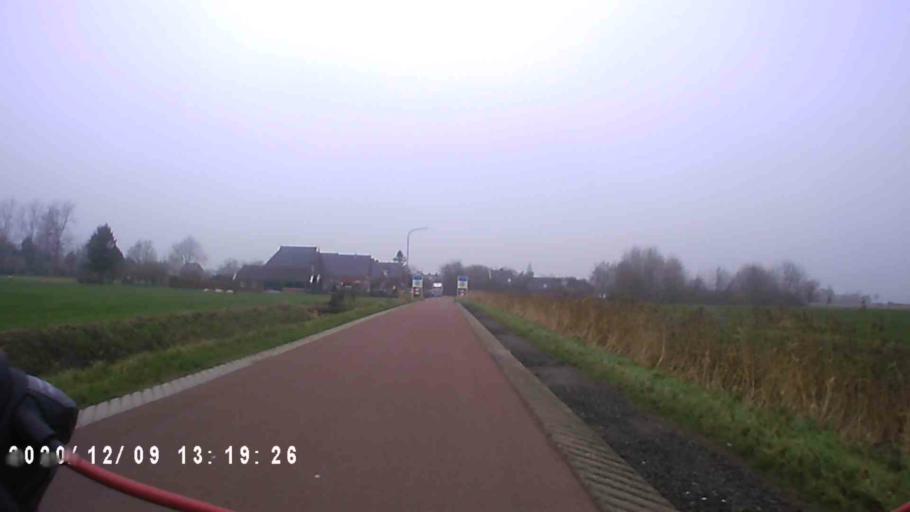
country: NL
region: Groningen
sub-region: Gemeente Groningen
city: Oosterpark
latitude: 53.2566
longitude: 6.5913
